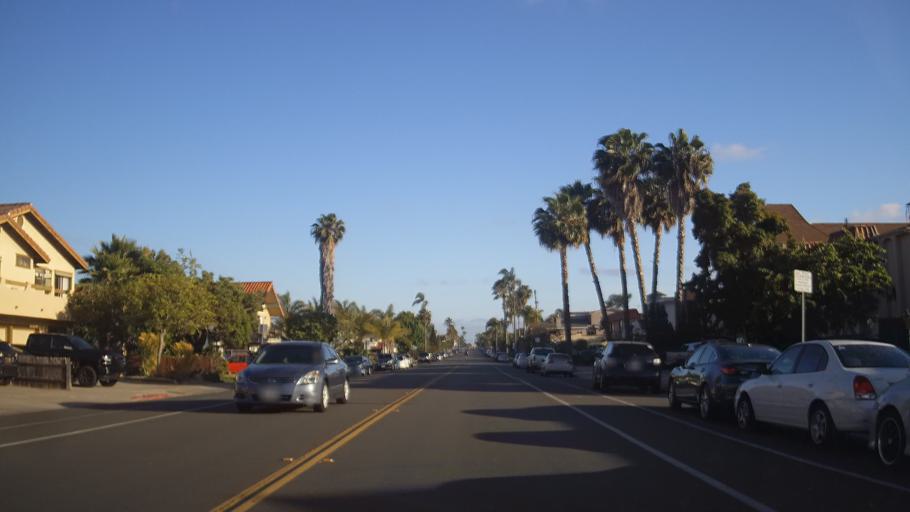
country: US
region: California
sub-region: San Diego County
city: San Diego
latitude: 32.7602
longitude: -117.1327
